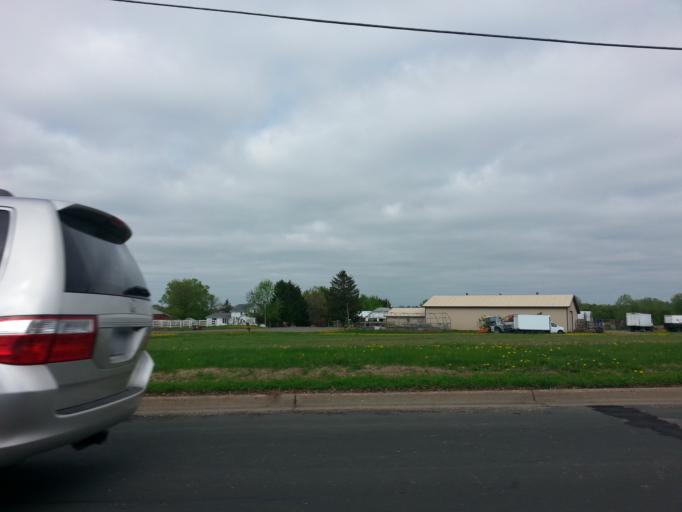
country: US
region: Minnesota
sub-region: Washington County
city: Woodbury
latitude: 44.9360
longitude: -92.9762
